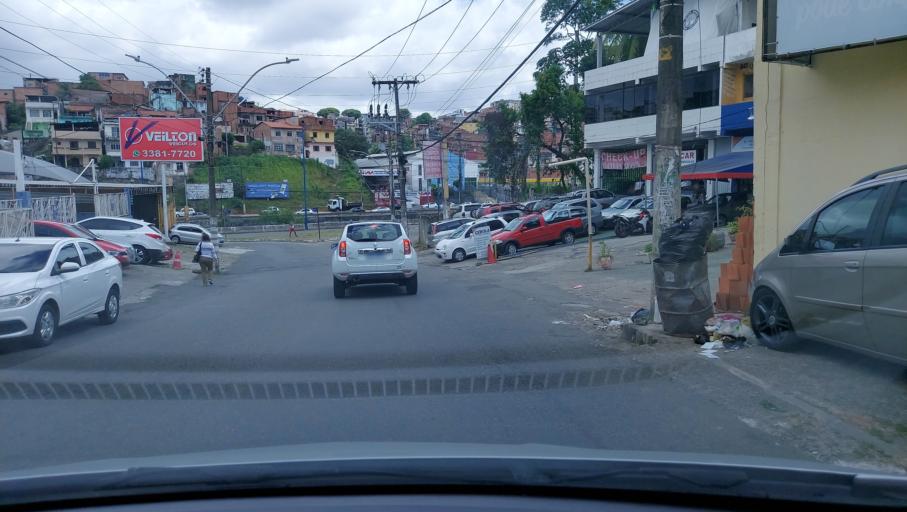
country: BR
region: Bahia
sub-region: Salvador
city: Salvador
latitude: -12.9690
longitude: -38.4877
